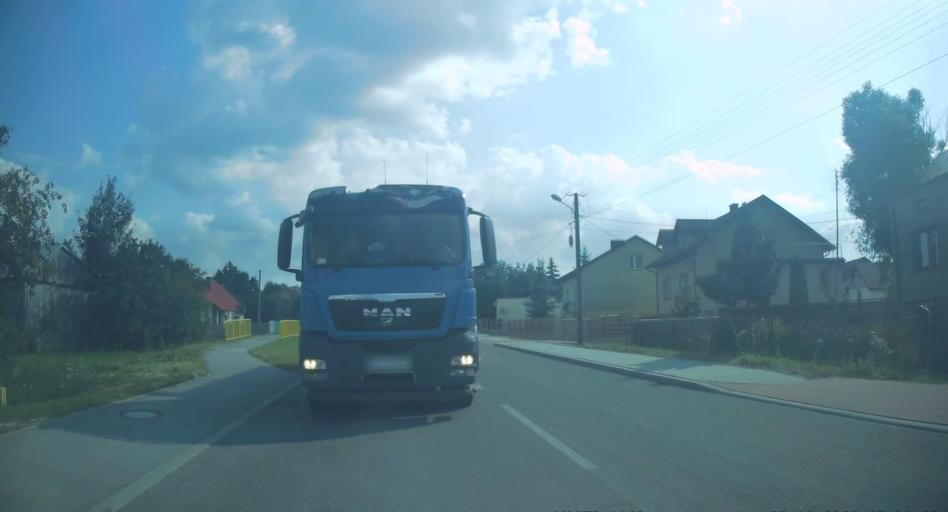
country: PL
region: Swietokrzyskie
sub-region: Powiat konecki
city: Radoszyce
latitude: 51.0410
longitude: 20.2828
